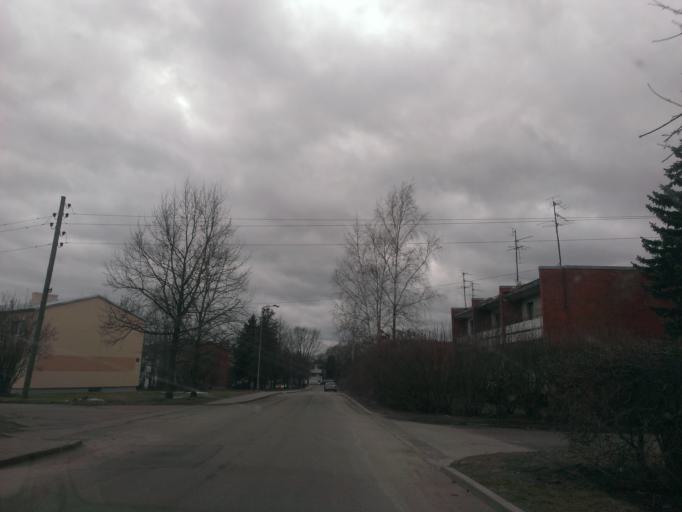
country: LV
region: Salaspils
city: Salaspils
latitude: 56.8586
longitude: 24.3541
